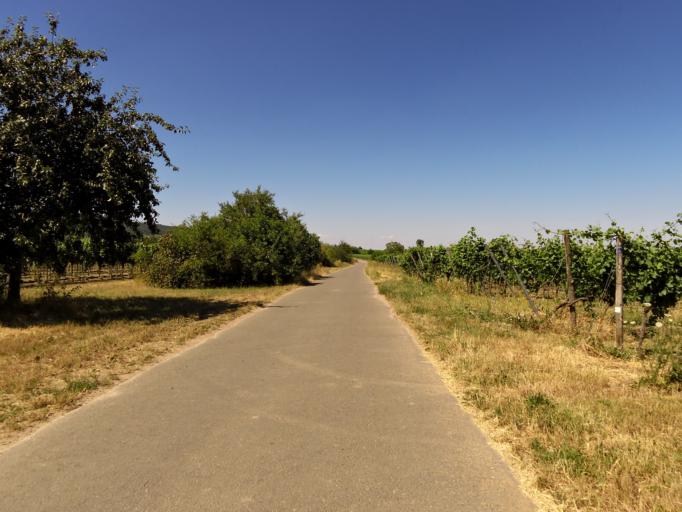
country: DE
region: Rheinland-Pfalz
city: Ruppertsberg
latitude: 49.3924
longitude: 8.1903
